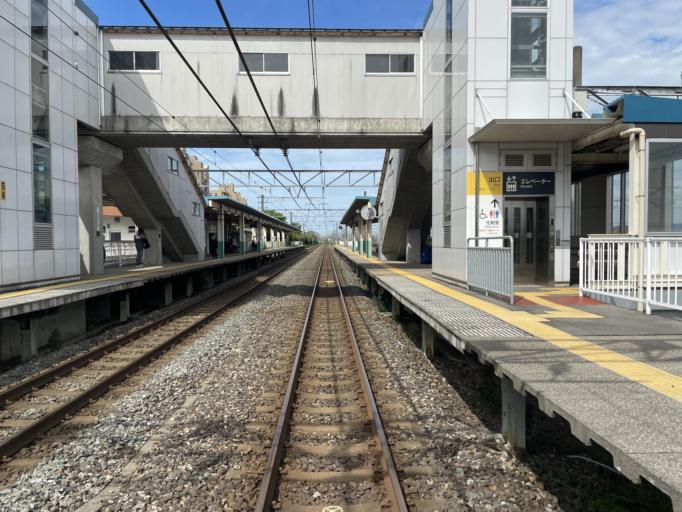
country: JP
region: Niigata
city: Kameda-honcho
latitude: 37.9089
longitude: 139.1090
